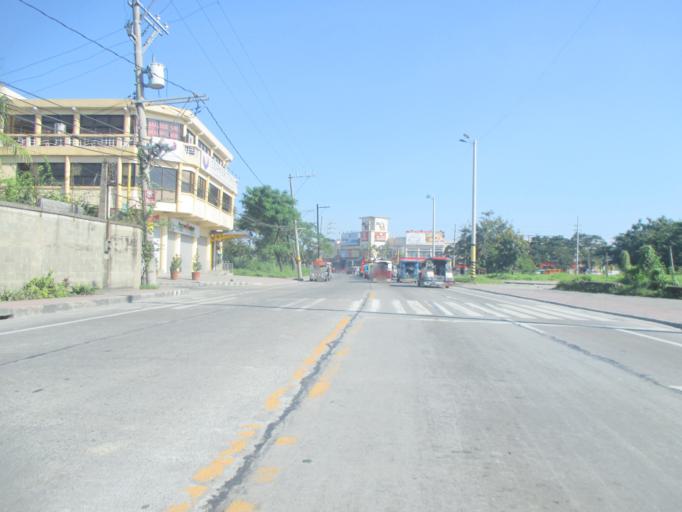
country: PH
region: Metro Manila
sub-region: Marikina
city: Calumpang
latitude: 14.6335
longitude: 121.1017
